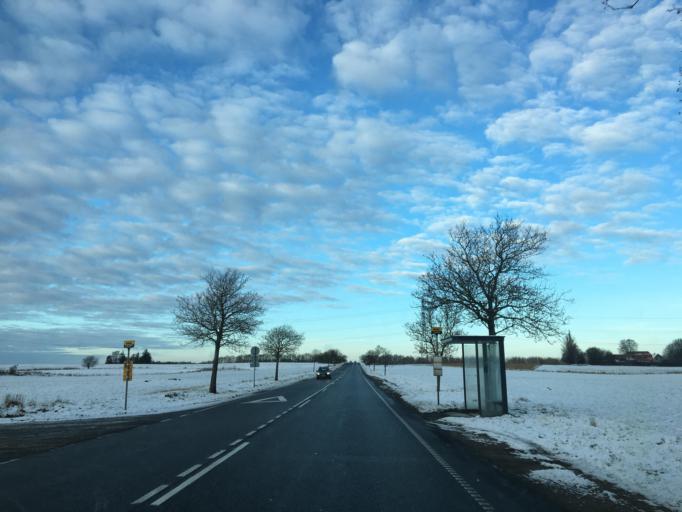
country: DK
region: Zealand
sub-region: Koge Kommune
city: Borup
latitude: 55.4520
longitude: 11.9863
